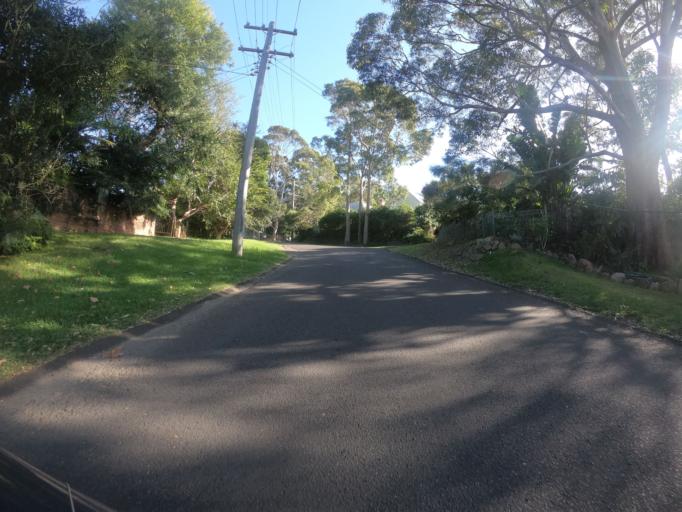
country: AU
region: New South Wales
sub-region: Wollongong
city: Bulli
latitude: -34.3125
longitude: 150.9174
